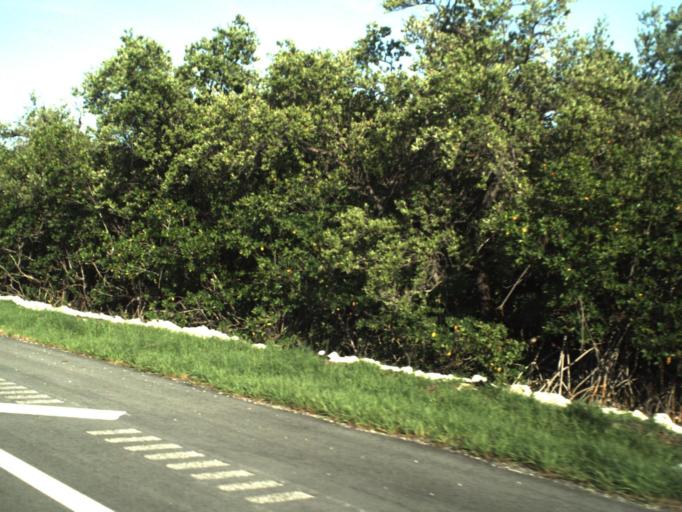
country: US
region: Florida
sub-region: Monroe County
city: Marathon
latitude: 24.7500
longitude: -80.9740
